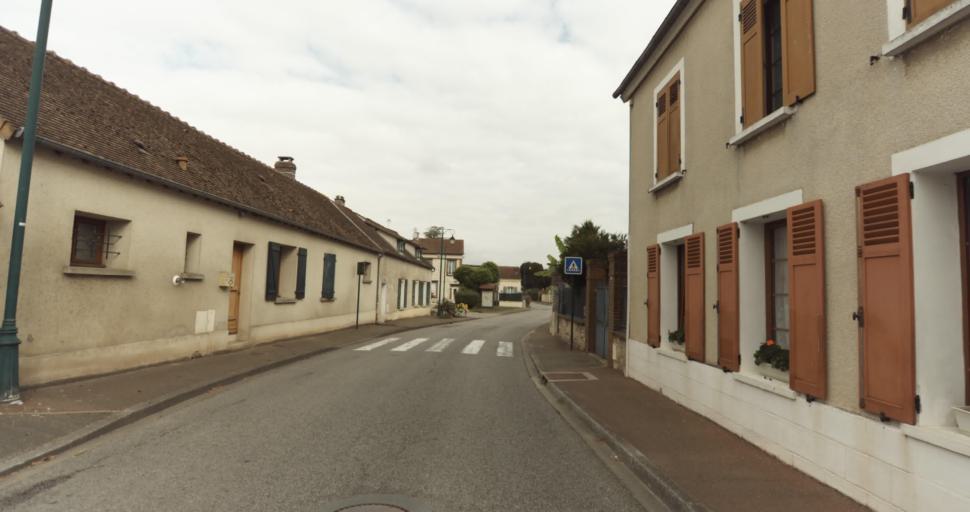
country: FR
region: Haute-Normandie
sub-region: Departement de l'Eure
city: Garennes-sur-Eure
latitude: 48.9113
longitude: 1.4386
